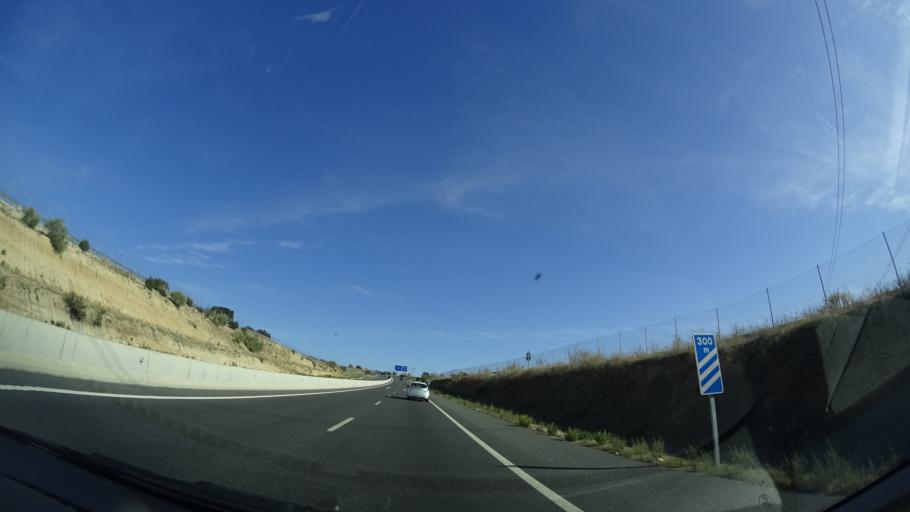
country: ES
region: Madrid
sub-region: Provincia de Madrid
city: Majadahonda
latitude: 40.4798
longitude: -3.9061
